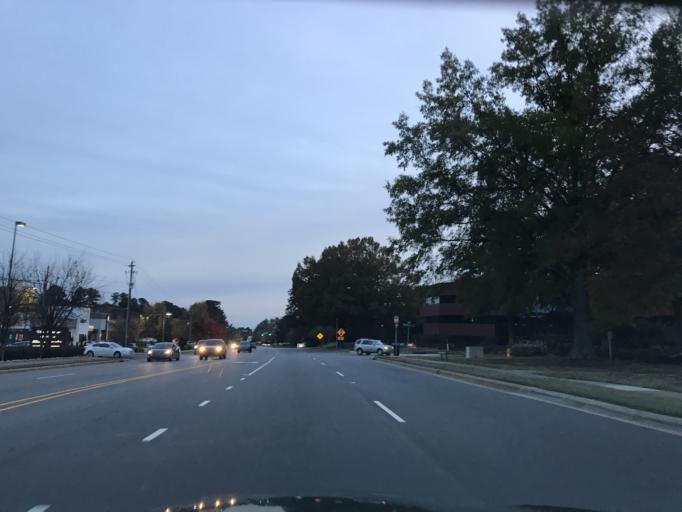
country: US
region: North Carolina
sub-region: Wake County
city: West Raleigh
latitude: 35.8664
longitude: -78.6206
